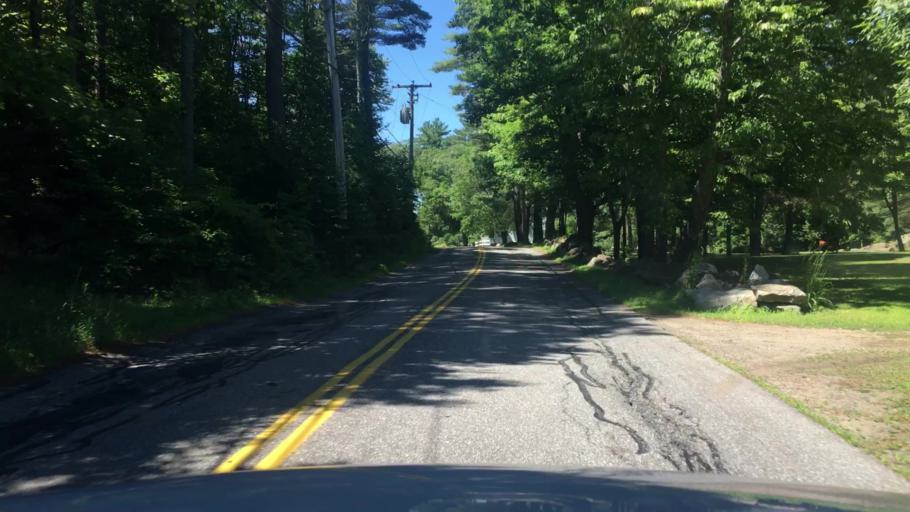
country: US
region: New Hampshire
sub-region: Merrimack County
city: Boscawen
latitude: 43.2654
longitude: -71.6117
